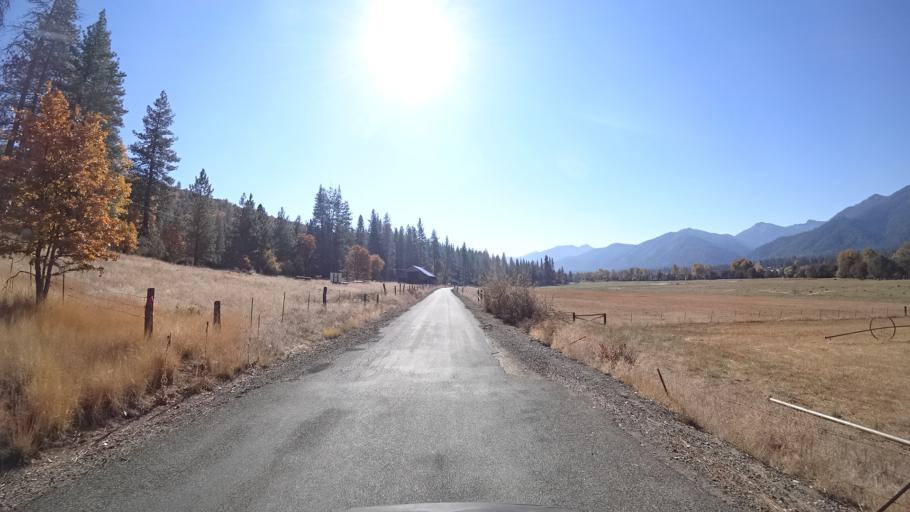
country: US
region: California
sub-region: Siskiyou County
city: Yreka
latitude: 41.5884
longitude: -122.9564
